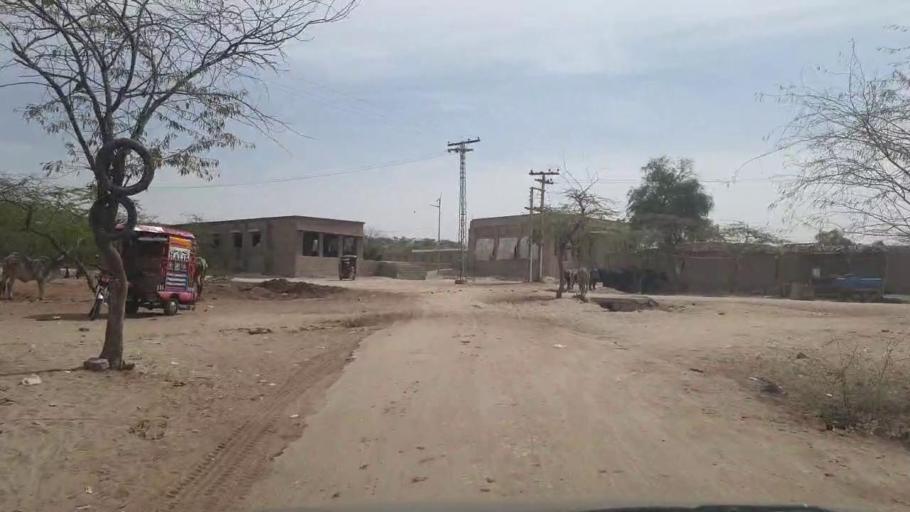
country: PK
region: Sindh
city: Umarkot
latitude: 25.2215
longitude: 69.7148
